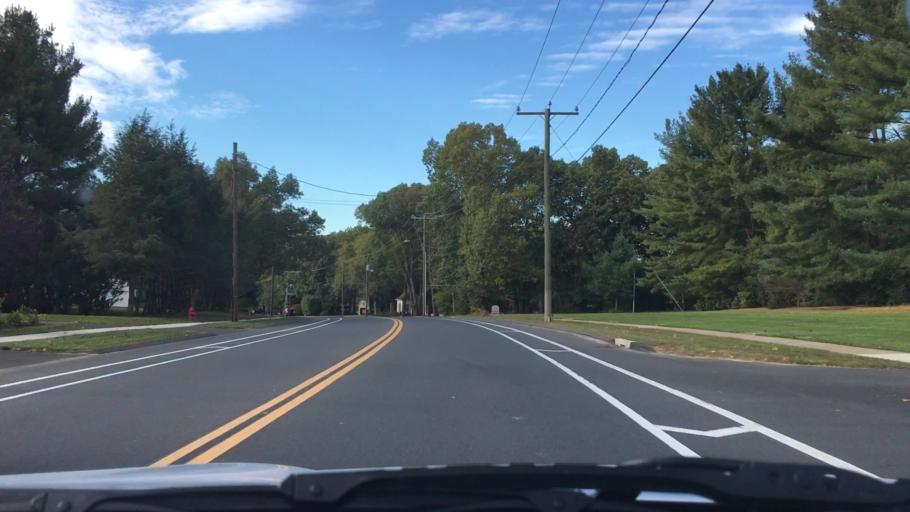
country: US
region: Massachusetts
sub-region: Hampden County
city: Longmeadow
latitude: 42.0642
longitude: -72.5521
